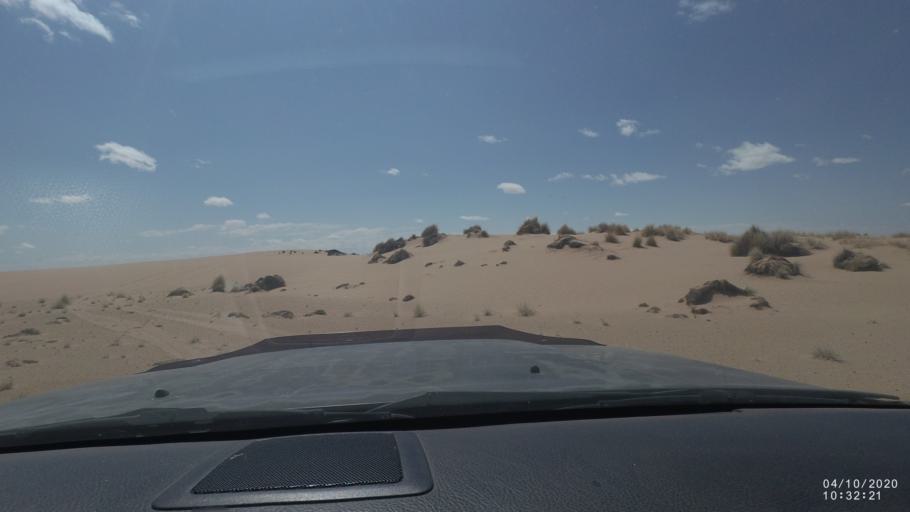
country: BO
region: Oruro
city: Poopo
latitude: -18.7047
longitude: -67.4825
